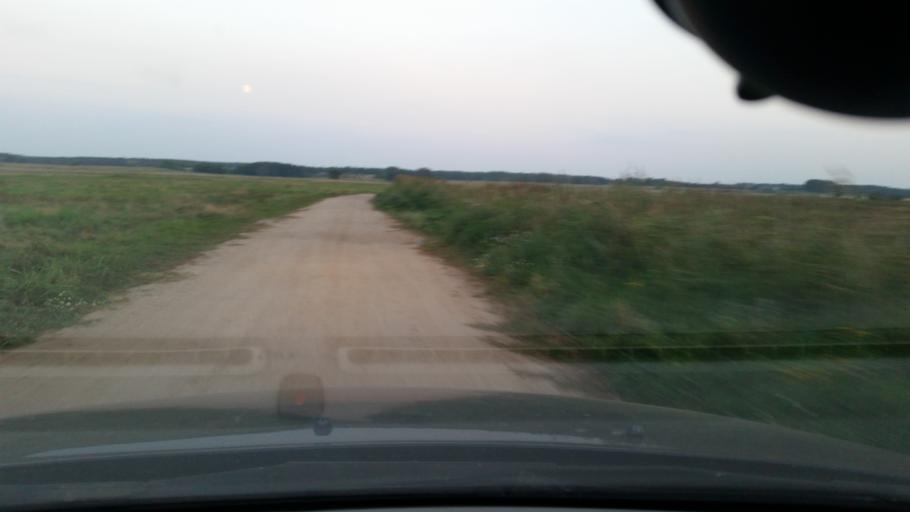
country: PL
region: Pomeranian Voivodeship
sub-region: Powiat wejherowski
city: Choczewo
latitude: 54.7880
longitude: 17.7945
